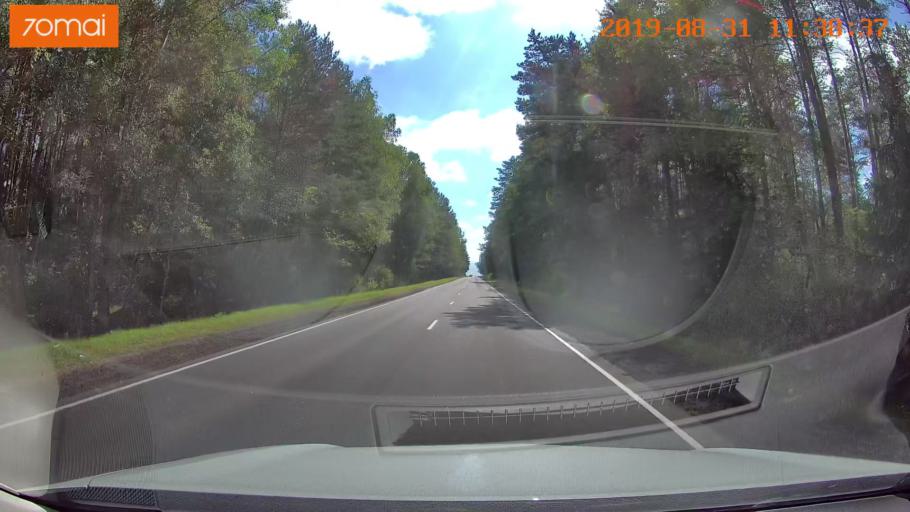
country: BY
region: Mogilev
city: Cherykaw
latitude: 53.6382
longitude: 31.2771
